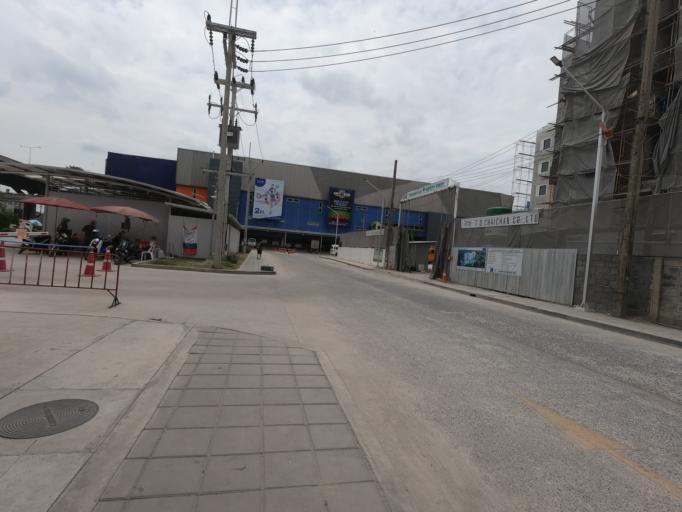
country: TH
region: Bangkok
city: Sai Mai
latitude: 13.9580
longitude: 100.6391
